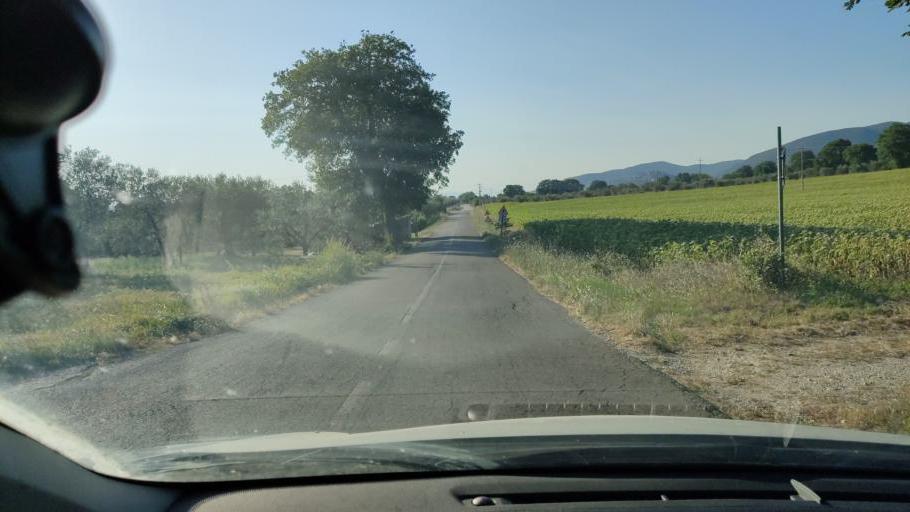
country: IT
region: Umbria
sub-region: Provincia di Terni
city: Lugnano in Teverina
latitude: 42.5465
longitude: 12.3511
